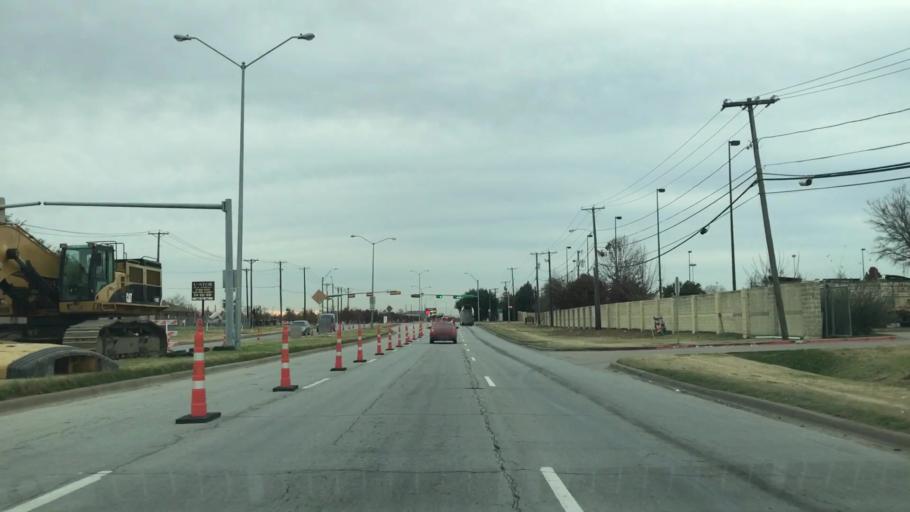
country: US
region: Texas
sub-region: Dallas County
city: Farmers Branch
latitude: 32.8567
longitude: -96.8803
